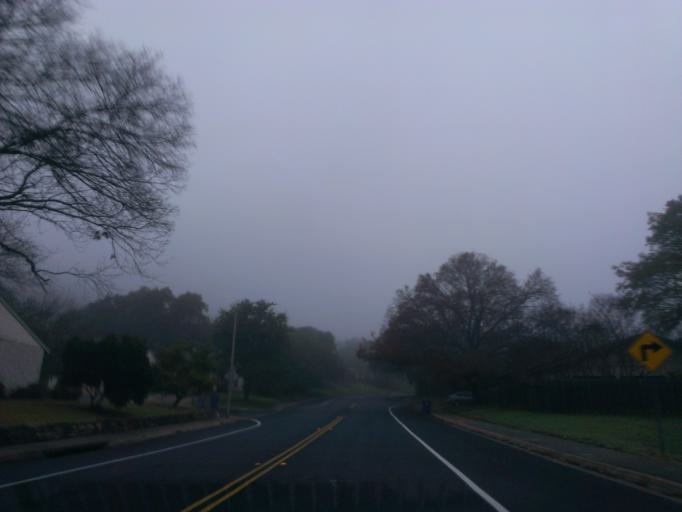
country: US
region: Texas
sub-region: Williamson County
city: Jollyville
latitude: 30.3734
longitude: -97.7890
